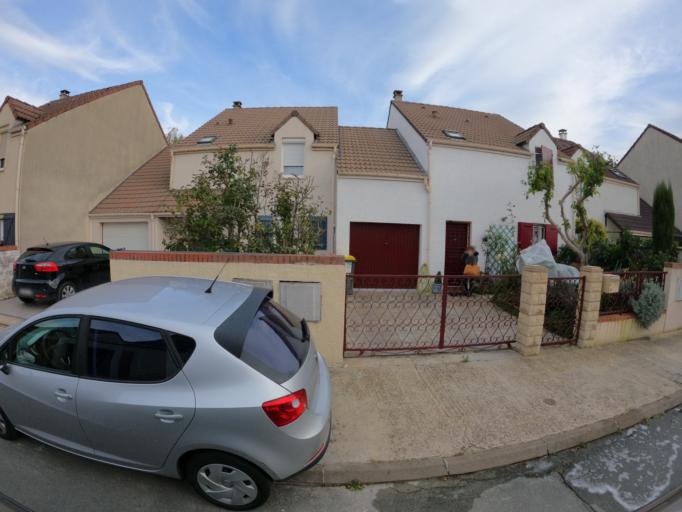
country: FR
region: Ile-de-France
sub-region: Departement de Seine-et-Marne
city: Emerainville
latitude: 48.8014
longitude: 2.6224
